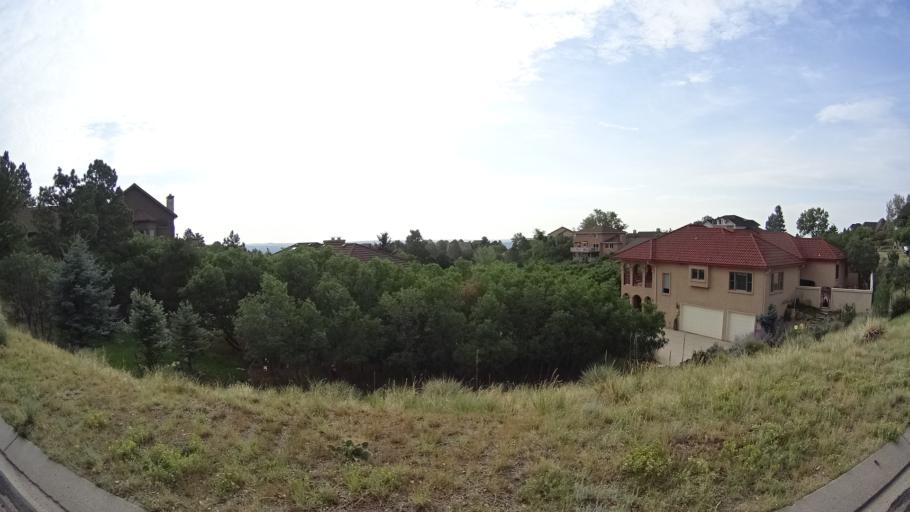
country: US
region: Colorado
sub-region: El Paso County
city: Air Force Academy
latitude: 38.9380
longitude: -104.8666
